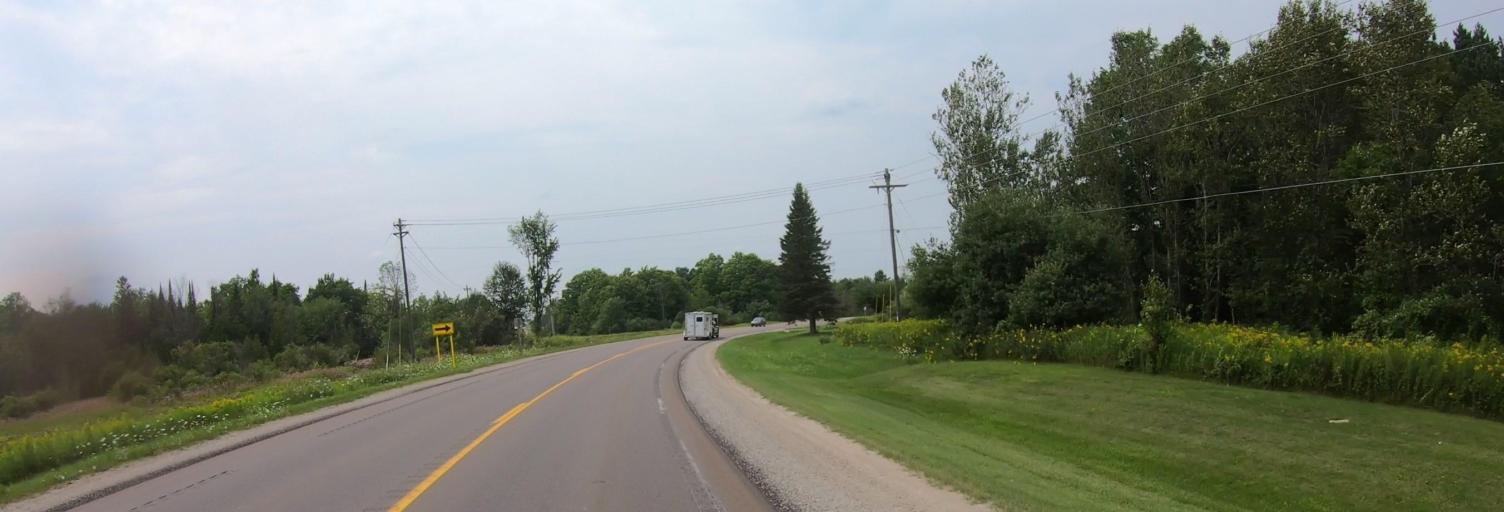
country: US
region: Michigan
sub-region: Alger County
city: Munising
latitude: 46.3477
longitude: -86.9471
